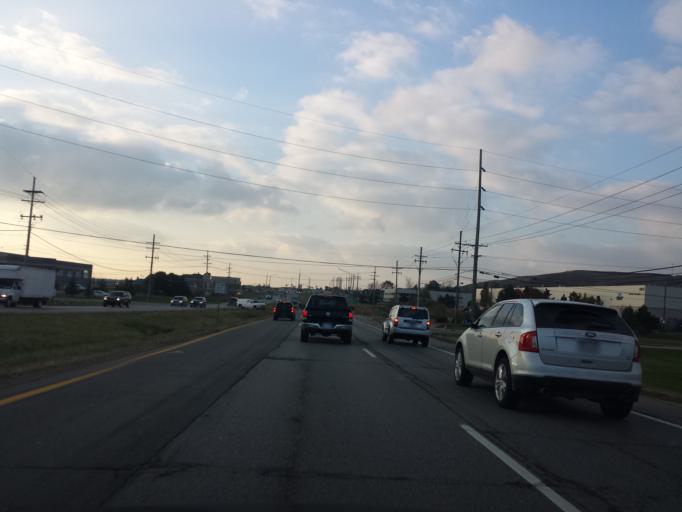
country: US
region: Michigan
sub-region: Oakland County
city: Auburn Hills
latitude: 42.7129
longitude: -83.2428
